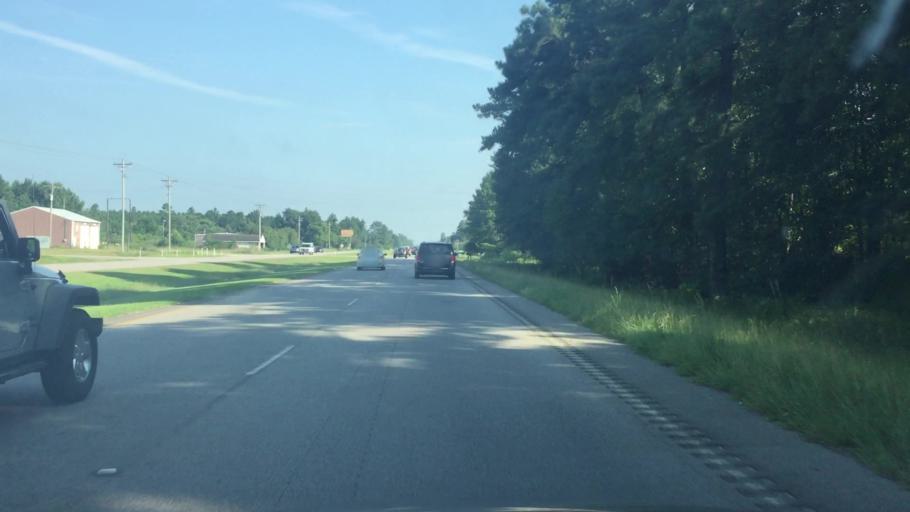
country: US
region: South Carolina
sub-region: Horry County
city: Little River
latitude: 33.9561
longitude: -78.7359
